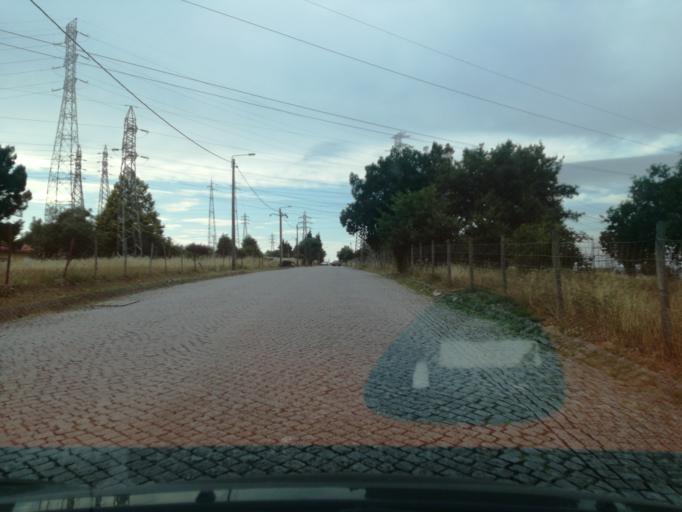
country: PT
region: Porto
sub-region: Maia
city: Maia
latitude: 41.2287
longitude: -8.6059
